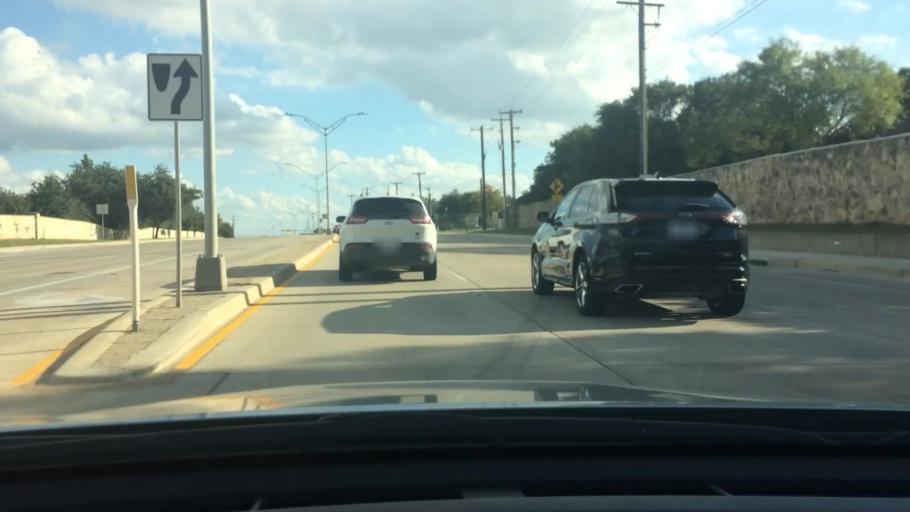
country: US
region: Texas
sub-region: Bexar County
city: Hollywood Park
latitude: 29.6117
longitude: -98.4209
